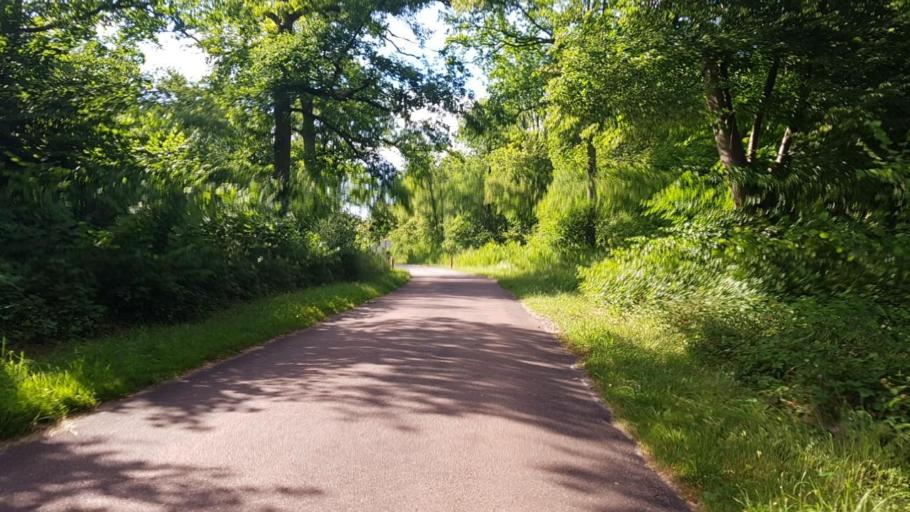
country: FR
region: Picardie
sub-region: Departement de l'Oise
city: Chamant
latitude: 49.1795
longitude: 2.6197
